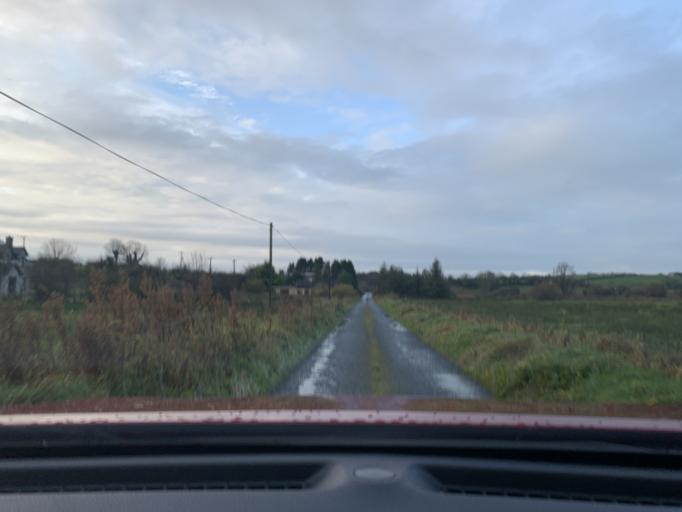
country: IE
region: Connaught
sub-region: Sligo
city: Ballymote
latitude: 54.0447
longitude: -8.5489
